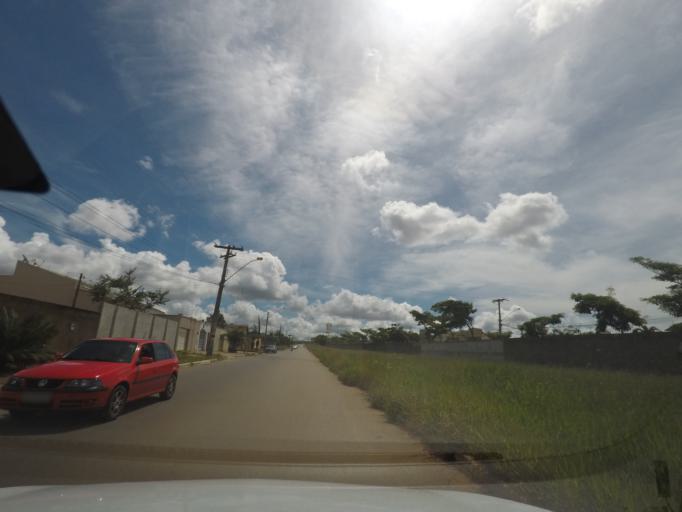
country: BR
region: Goias
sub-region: Goiania
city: Goiania
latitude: -16.7543
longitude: -49.3439
